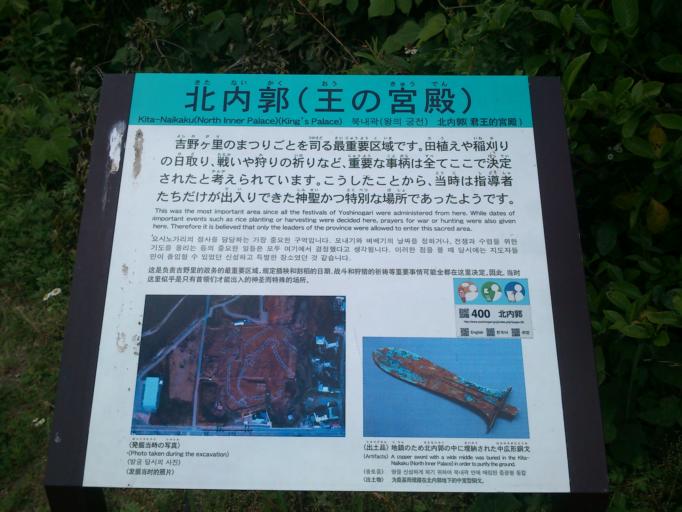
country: JP
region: Saga Prefecture
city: Kanzakimachi-kanzaki
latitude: 33.3228
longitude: 130.3893
